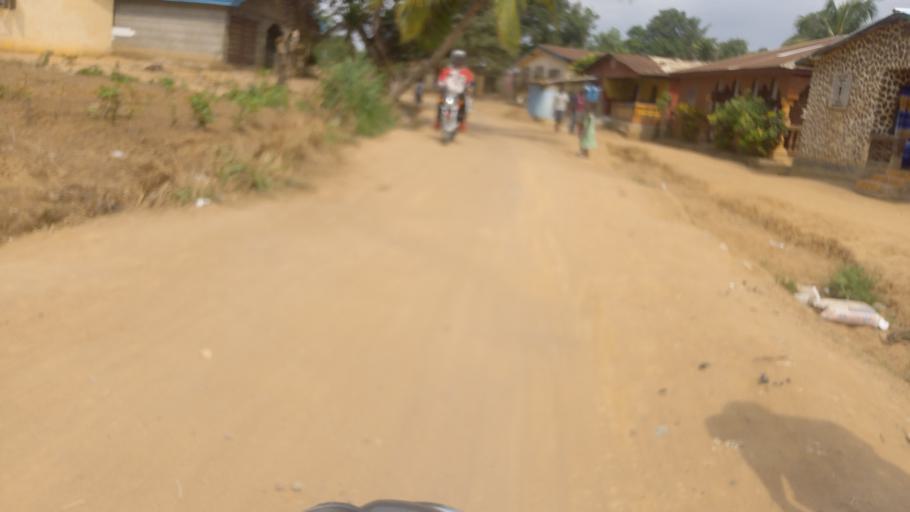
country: SL
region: Western Area
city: Waterloo
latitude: 8.3232
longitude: -13.0579
